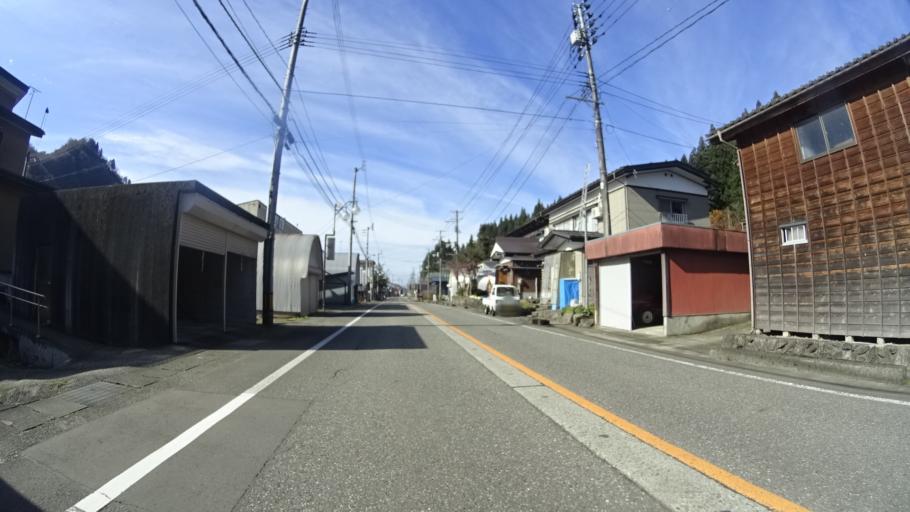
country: JP
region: Niigata
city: Muikamachi
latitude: 37.2073
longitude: 139.0647
